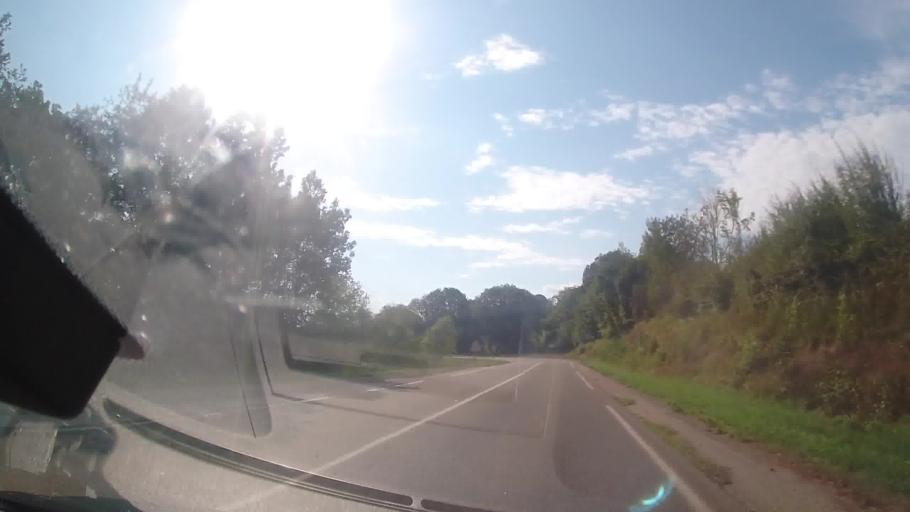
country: FR
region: Franche-Comte
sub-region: Departement du Jura
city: Clairvaux-les-Lacs
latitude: 46.5996
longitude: 5.8670
